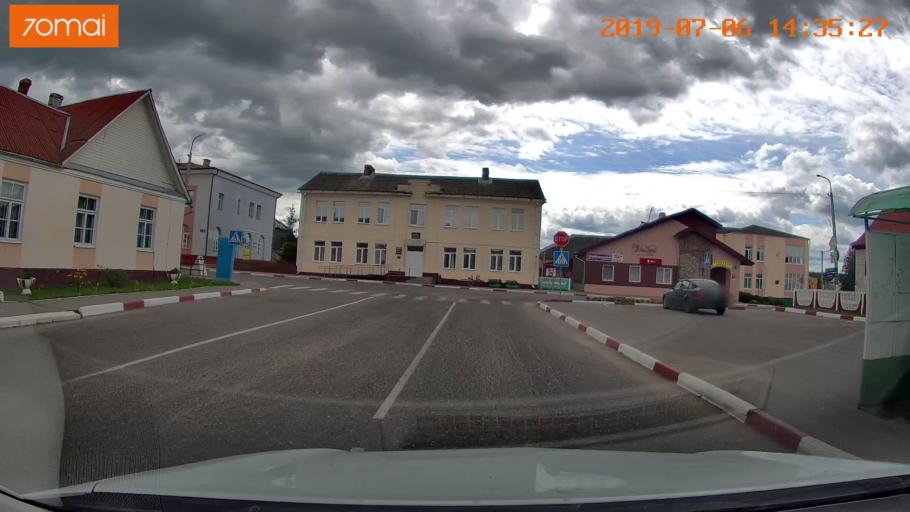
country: BY
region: Minsk
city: Ivyanyets
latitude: 53.8915
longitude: 26.7404
